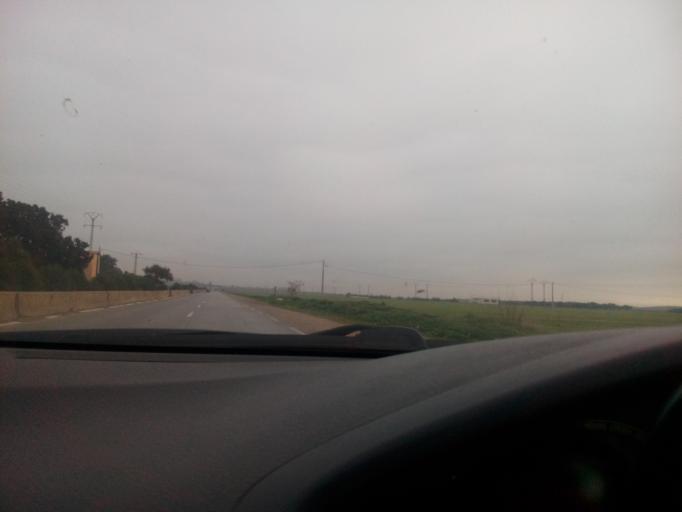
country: DZ
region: Oran
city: Bou Tlelis
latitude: 35.5498
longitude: -0.9555
